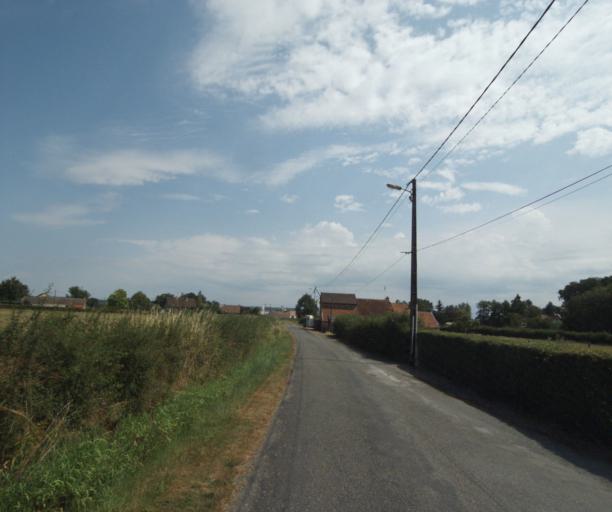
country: FR
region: Bourgogne
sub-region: Departement de Saone-et-Loire
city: Gueugnon
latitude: 46.6136
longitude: 4.0379
